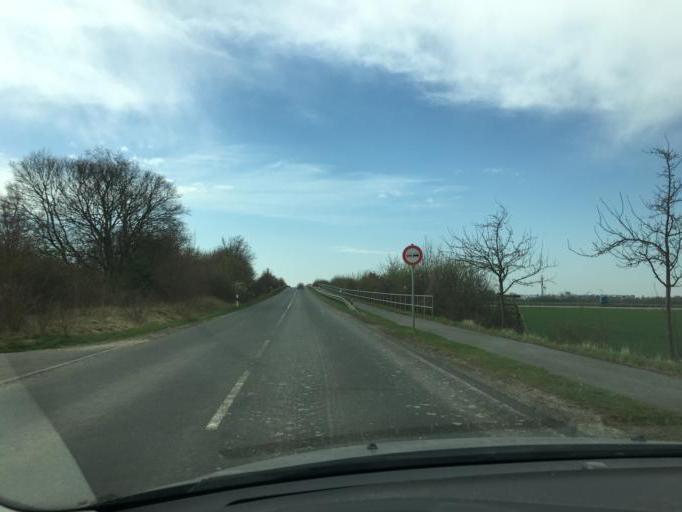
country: DE
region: Saxony
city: Taucha
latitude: 51.3599
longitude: 12.4914
